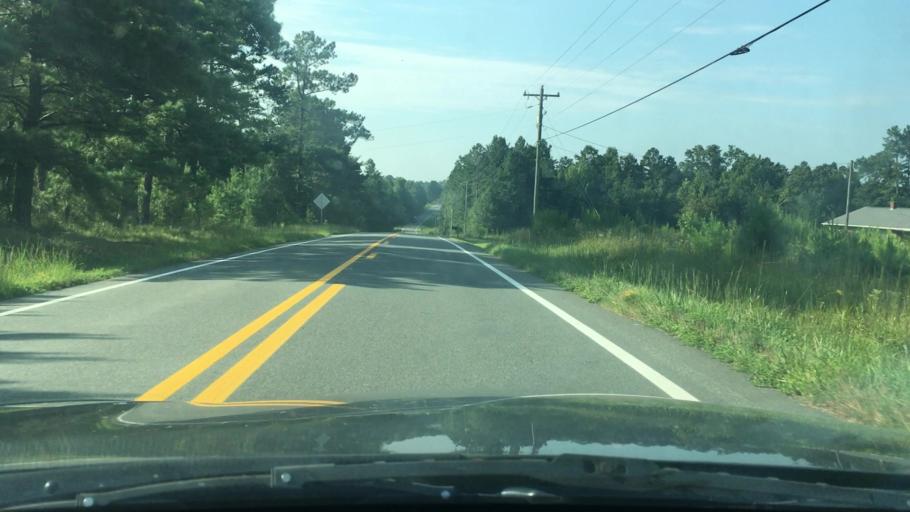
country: US
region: North Carolina
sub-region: Alamance County
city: Green Level
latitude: 36.2247
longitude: -79.3232
